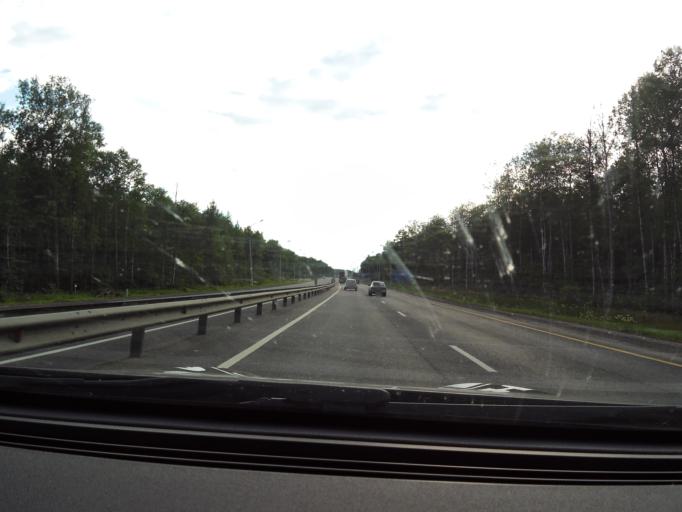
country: RU
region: Vladimir
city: Kameshkovo
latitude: 56.1958
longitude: 40.9759
